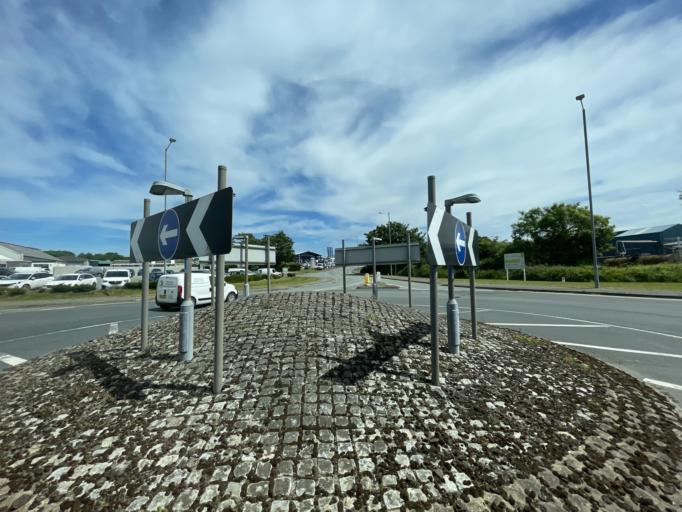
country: GB
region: Wales
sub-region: Anglesey
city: Llangefni
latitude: 53.2509
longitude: -4.3072
